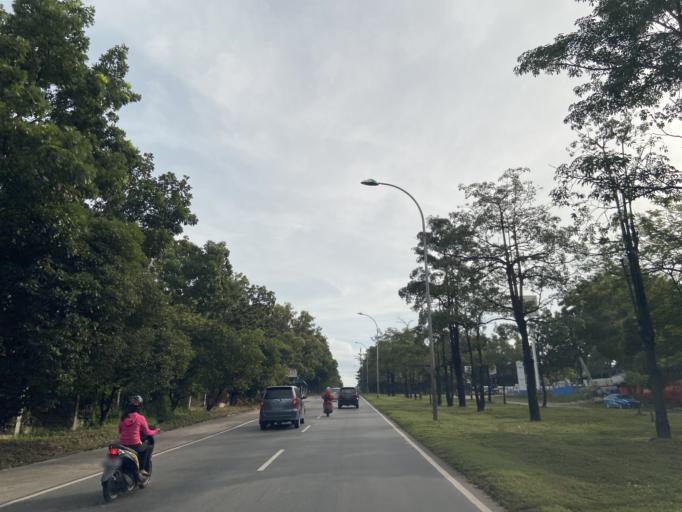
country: SG
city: Singapore
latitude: 1.1355
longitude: 104.0230
